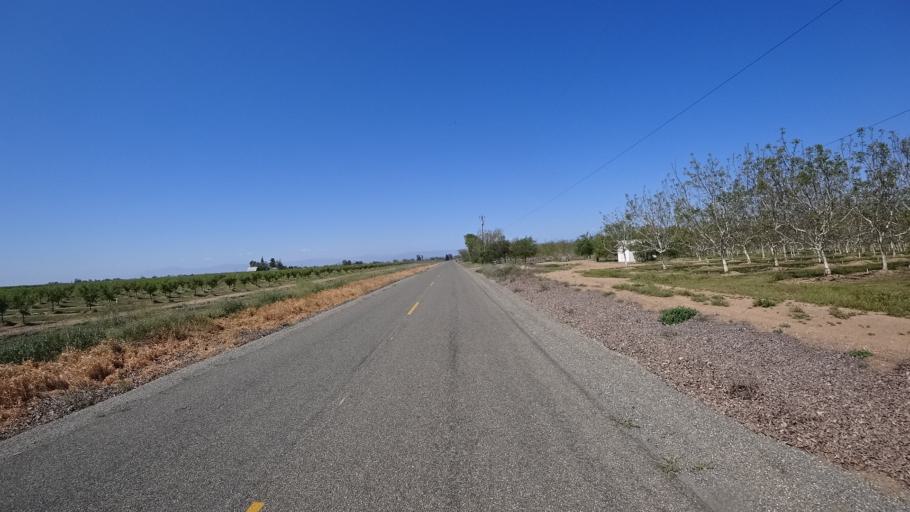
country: US
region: California
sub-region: Glenn County
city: Orland
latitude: 39.7870
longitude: -122.1612
